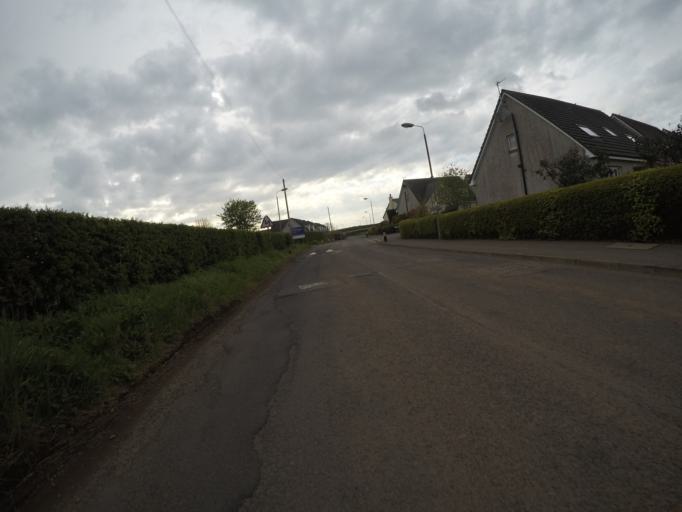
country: GB
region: Scotland
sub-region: East Ayrshire
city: Kilmaurs
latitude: 55.6395
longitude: -4.5396
